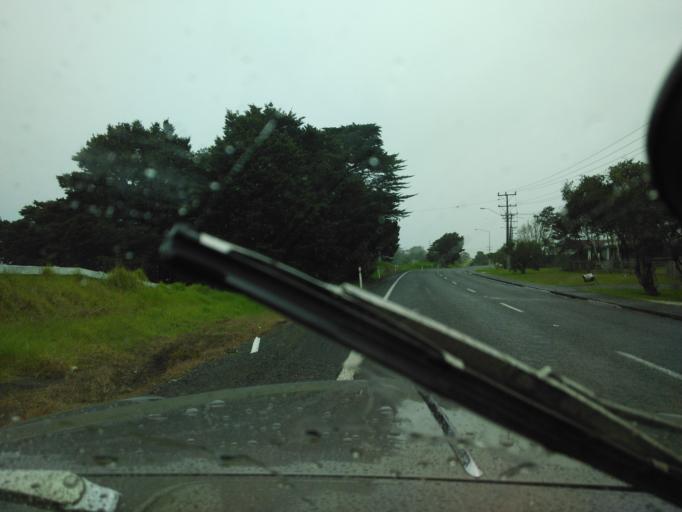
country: NZ
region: Auckland
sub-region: Auckland
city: Wellsford
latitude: -36.2992
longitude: 174.5144
